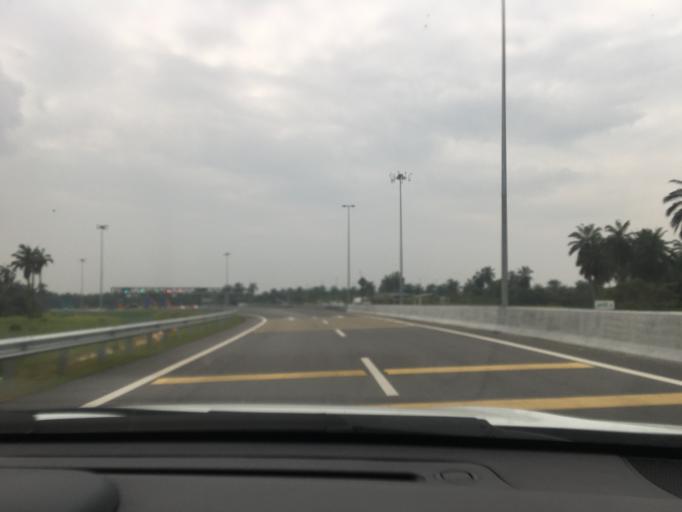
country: MY
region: Selangor
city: Klang
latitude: 3.1325
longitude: 101.3971
